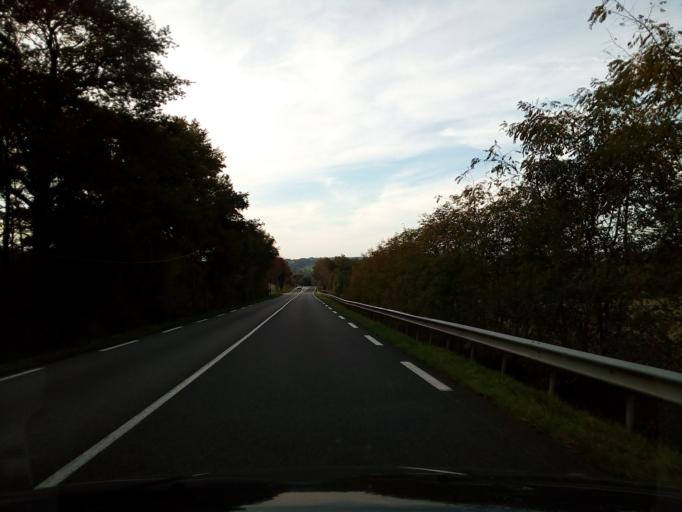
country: FR
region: Poitou-Charentes
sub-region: Departement de la Charente
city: Confolens
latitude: 46.0624
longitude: 0.6969
